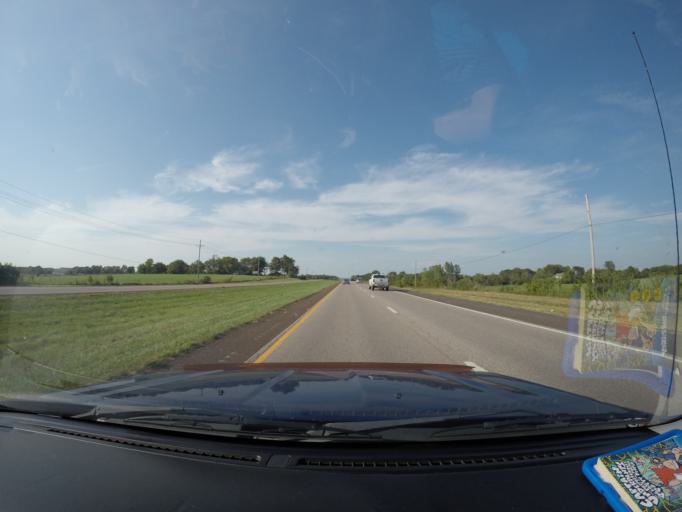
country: US
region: Kansas
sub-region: Leavenworth County
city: Lansing
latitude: 39.1910
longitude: -94.9003
